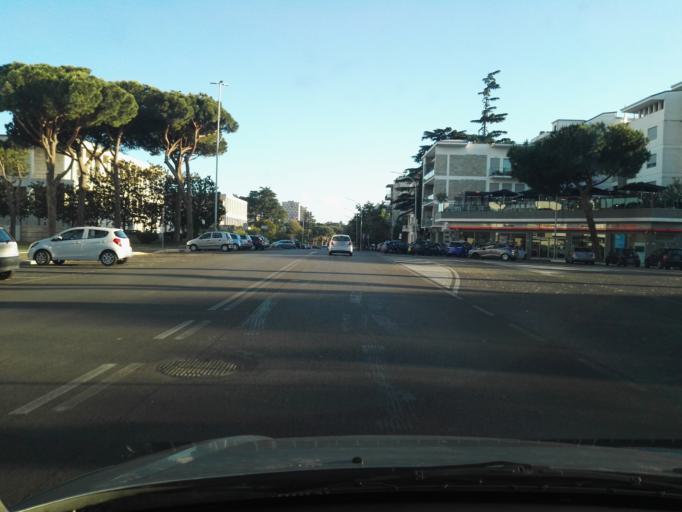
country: IT
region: Latium
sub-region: Citta metropolitana di Roma Capitale
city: Selcetta
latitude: 41.8310
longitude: 12.4751
